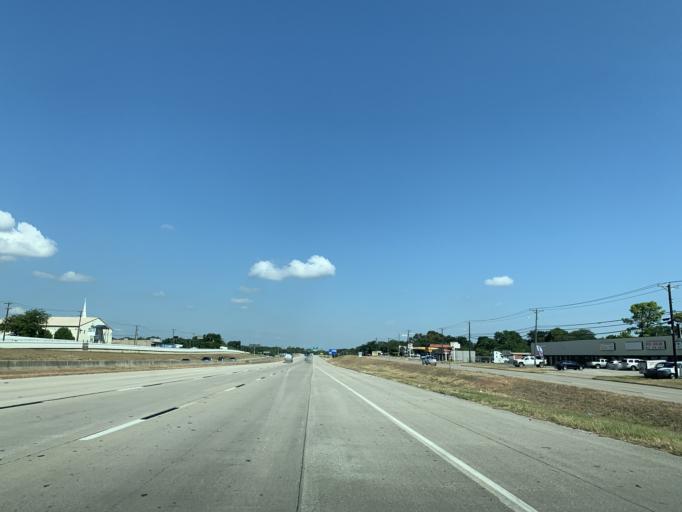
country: US
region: Texas
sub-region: Tarrant County
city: Azle
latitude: 32.8742
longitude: -97.5289
